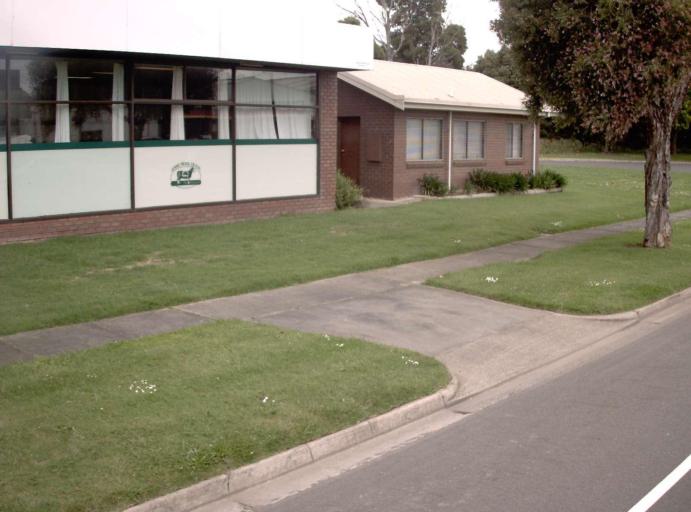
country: AU
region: Victoria
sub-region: Baw Baw
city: Warragul
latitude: -38.1664
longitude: 145.9404
